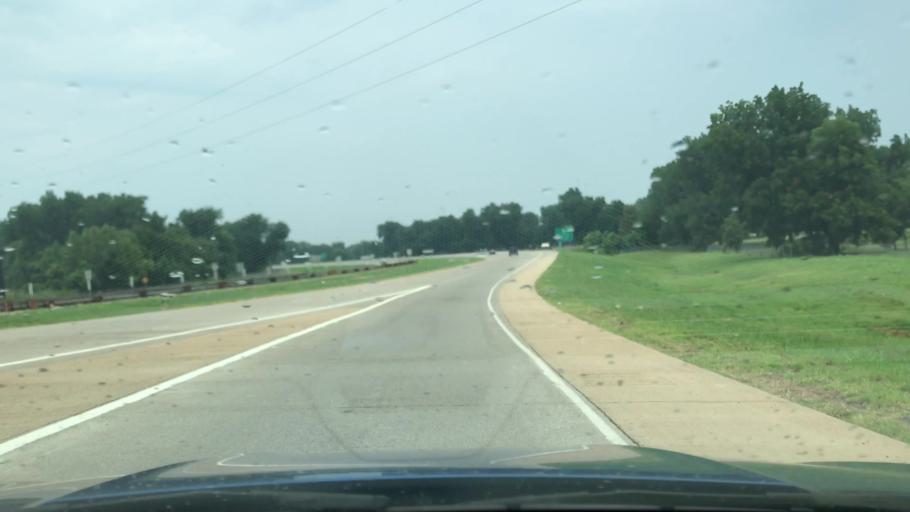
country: US
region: Louisiana
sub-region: Bossier Parish
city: Bossier City
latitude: 32.4032
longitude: -93.7143
